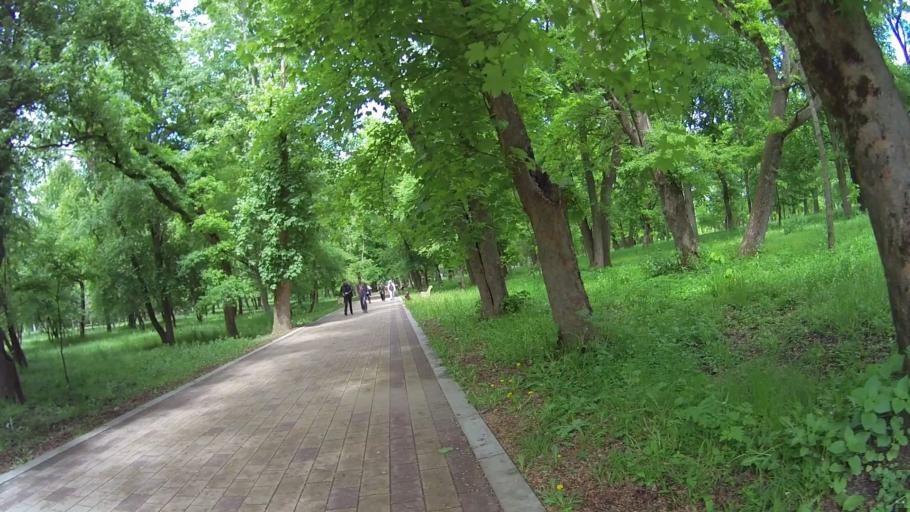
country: RU
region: Kabardino-Balkariya
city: Vol'nyy Aul
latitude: 43.4635
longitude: 43.5898
